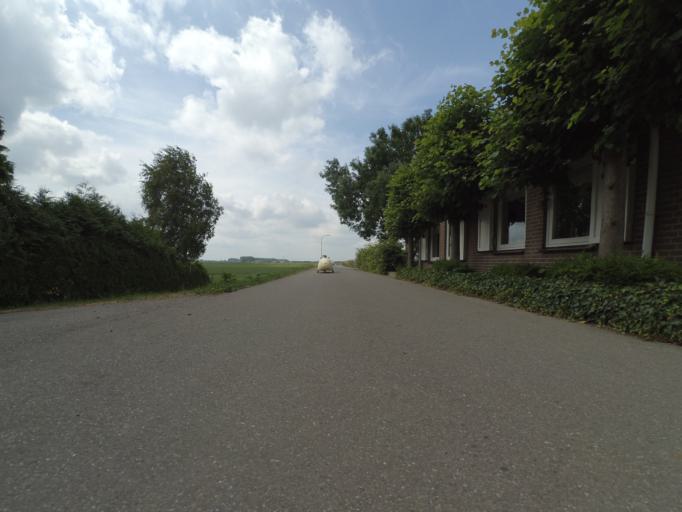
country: NL
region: North Brabant
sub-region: Gemeente Woudrichem
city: Almkerk
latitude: 51.7588
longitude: 4.9110
